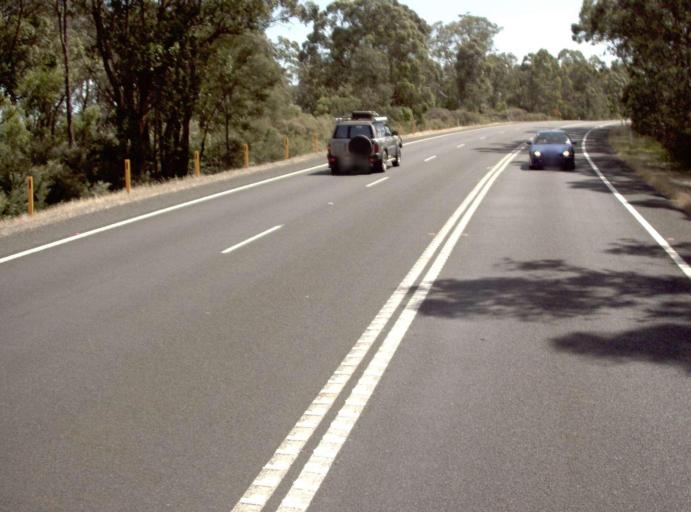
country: AU
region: Victoria
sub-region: East Gippsland
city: Bairnsdale
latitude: -37.9107
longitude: 147.3140
